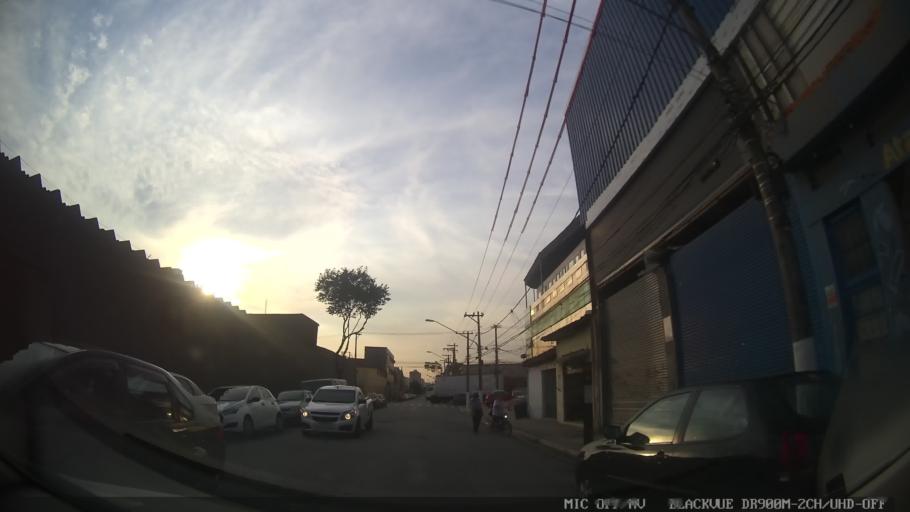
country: BR
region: Sao Paulo
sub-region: Sao Caetano Do Sul
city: Sao Caetano do Sul
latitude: -23.6008
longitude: -46.5873
